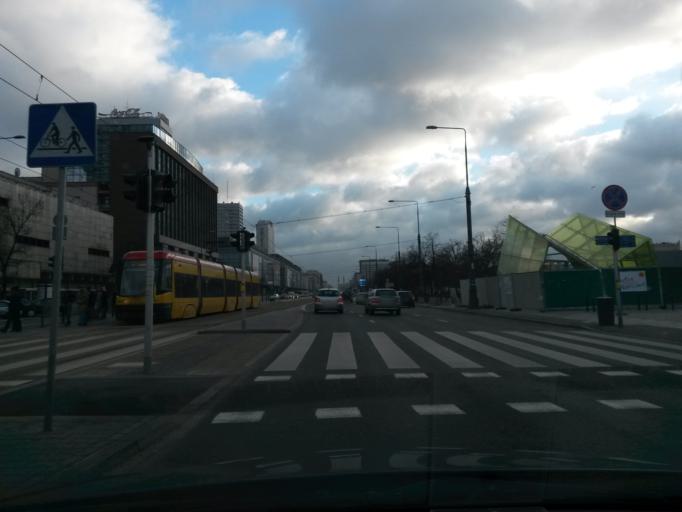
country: PL
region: Masovian Voivodeship
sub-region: Warszawa
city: Warsaw
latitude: 52.2351
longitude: 21.0085
